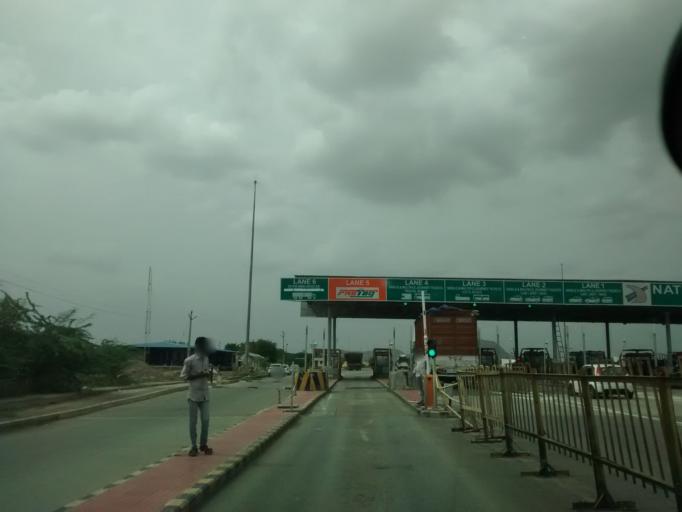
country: IN
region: Andhra Pradesh
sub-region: Kurnool
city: Ramapuram
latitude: 15.0612
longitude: 77.6300
